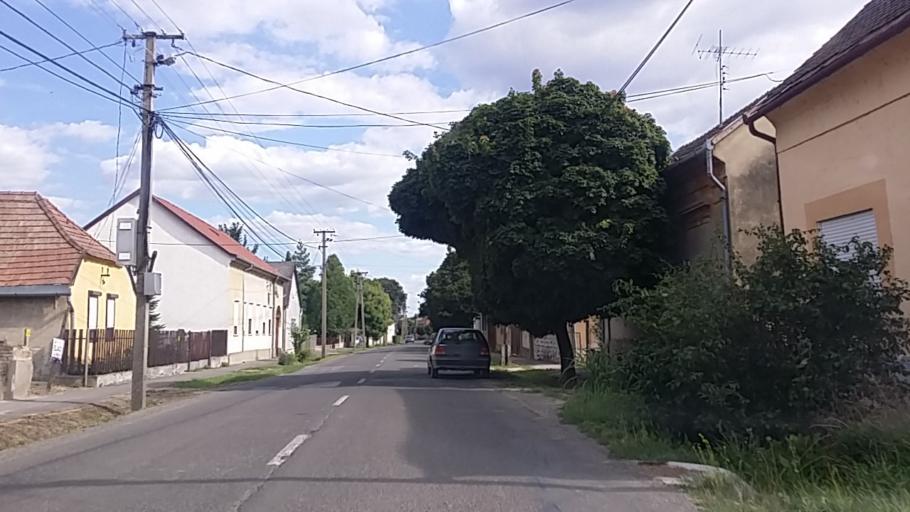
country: HU
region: Tolna
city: Dombovar
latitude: 46.3743
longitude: 18.1241
